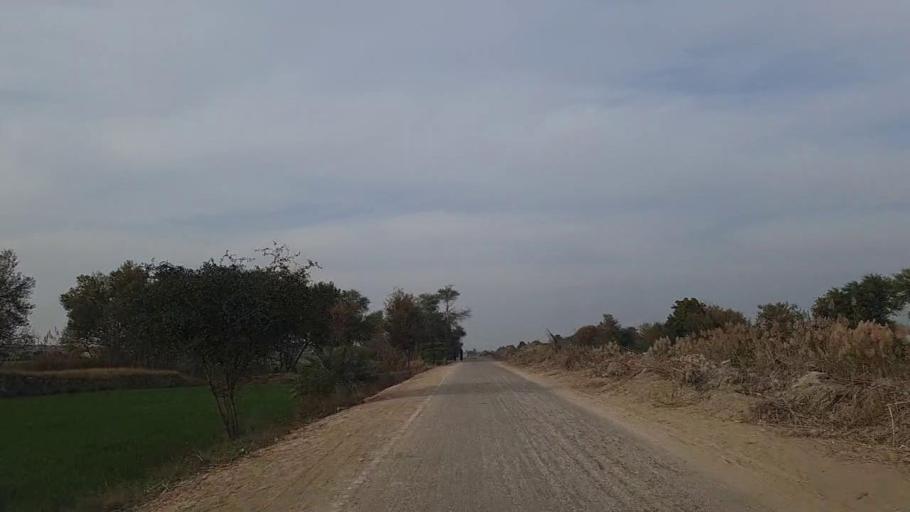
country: PK
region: Sindh
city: Daur
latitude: 26.4773
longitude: 68.4651
